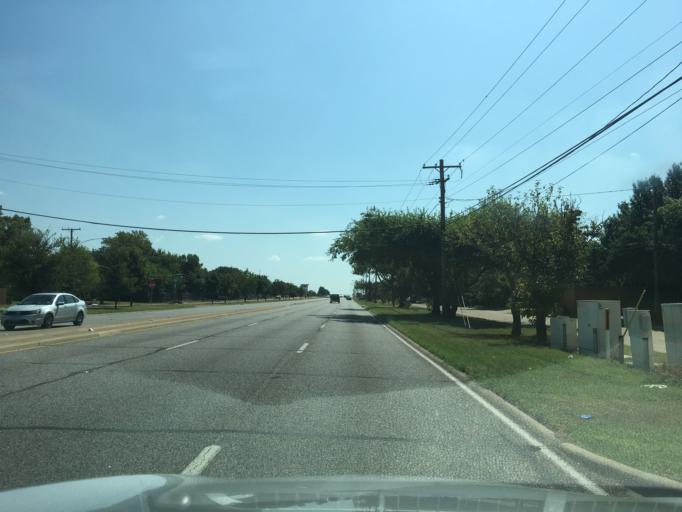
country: US
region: Texas
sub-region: Dallas County
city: Garland
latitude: 32.8642
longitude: -96.6919
